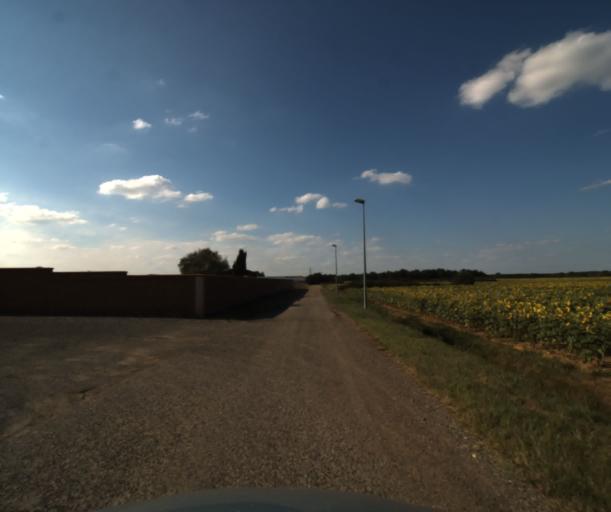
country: FR
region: Midi-Pyrenees
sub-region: Departement de la Haute-Garonne
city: Saint-Lys
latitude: 43.5079
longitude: 1.2005
